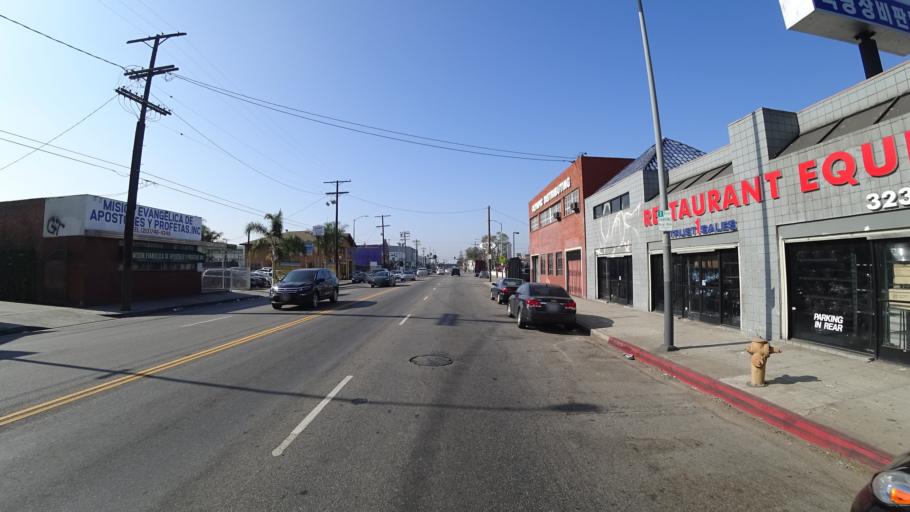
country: US
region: California
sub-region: Los Angeles County
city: Echo Park
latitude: 34.0416
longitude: -118.2917
